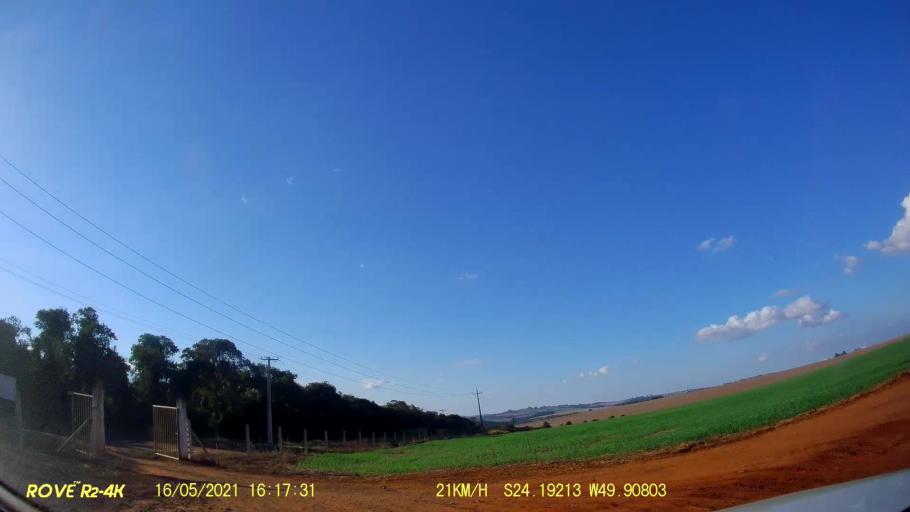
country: BR
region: Parana
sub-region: Jaguariaiva
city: Jaguariaiva
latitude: -24.1921
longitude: -49.9080
